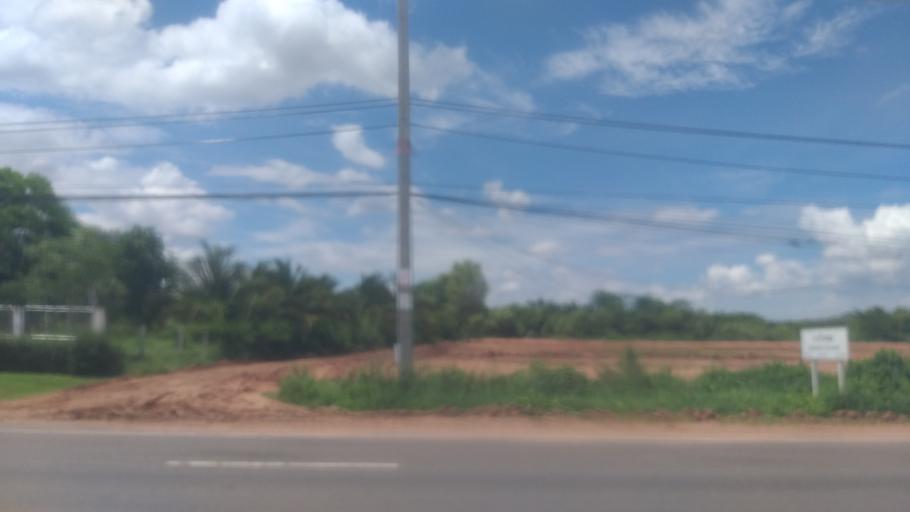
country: TH
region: Nakhon Ratchasima
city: Phra Thong Kham
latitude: 15.2965
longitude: 101.9851
